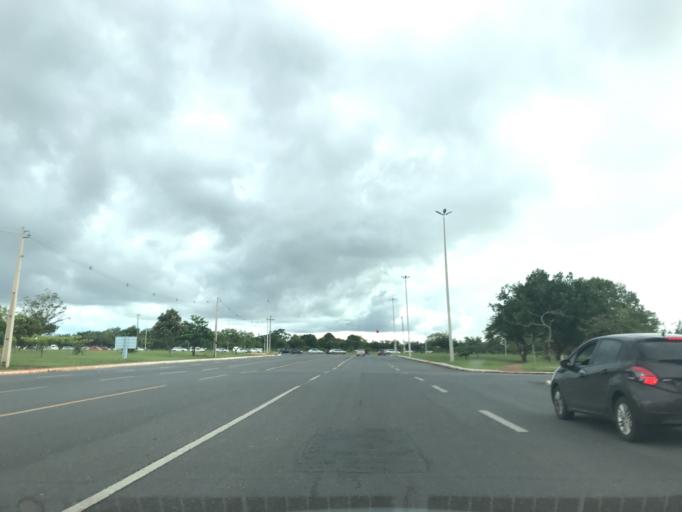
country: BR
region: Federal District
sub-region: Brasilia
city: Brasilia
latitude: -15.7787
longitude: -47.9220
